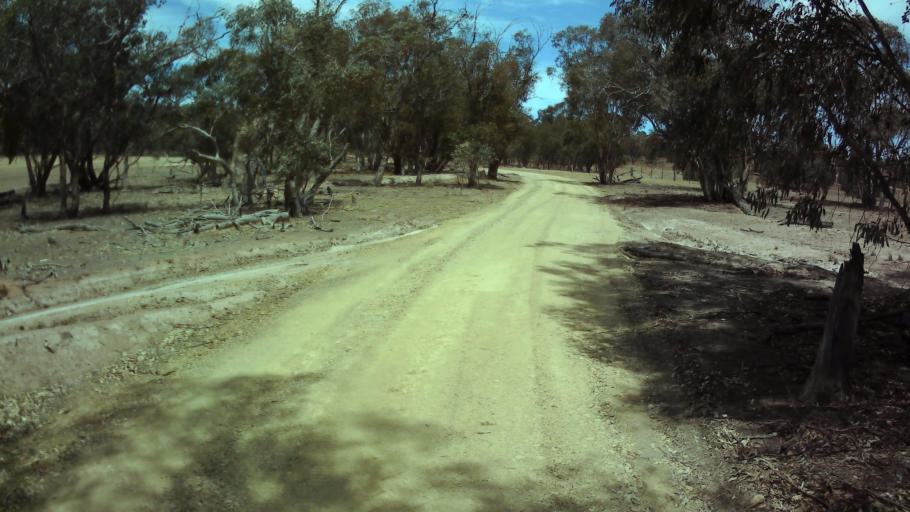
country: AU
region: New South Wales
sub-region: Weddin
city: Grenfell
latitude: -33.7846
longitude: 148.1522
